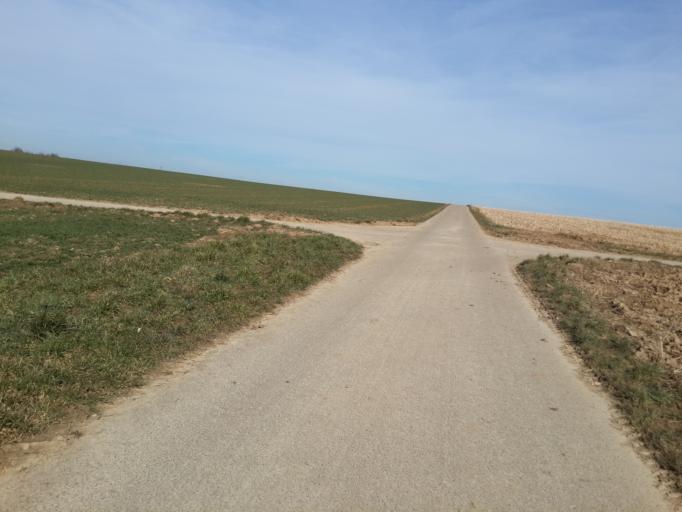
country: DE
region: Baden-Wuerttemberg
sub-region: Regierungsbezirk Stuttgart
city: Heilbronn
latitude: 49.1501
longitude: 9.1693
